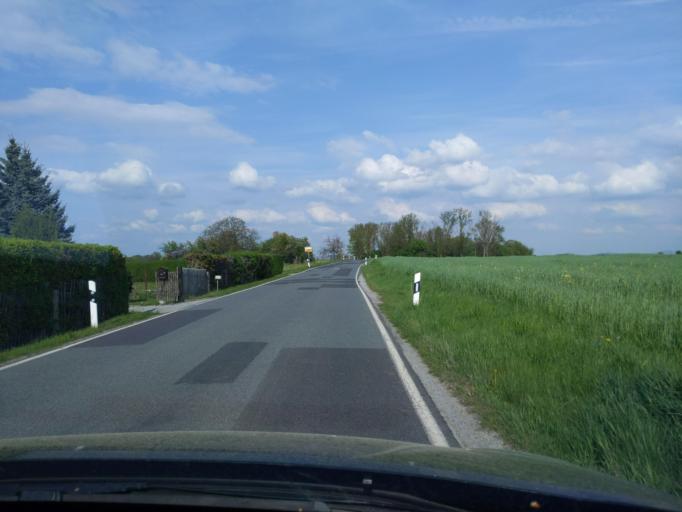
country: DE
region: Saxony
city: Kubschutz
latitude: 51.1976
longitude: 14.5101
